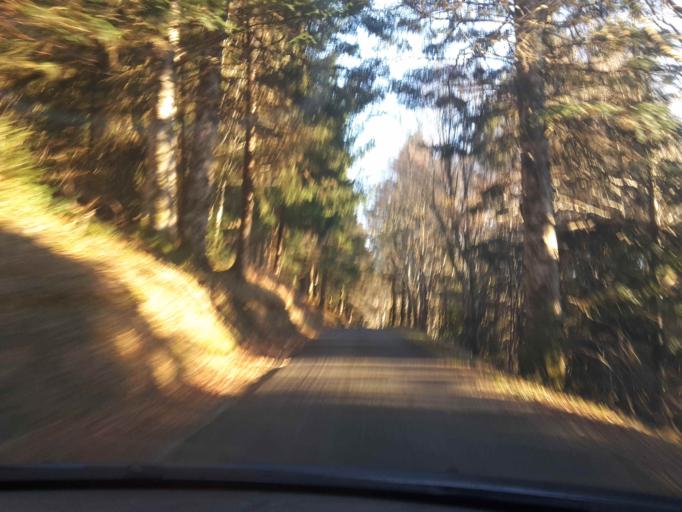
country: FR
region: Auvergne
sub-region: Departement du Cantal
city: Riom-es-Montagnes
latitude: 45.2255
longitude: 2.5668
